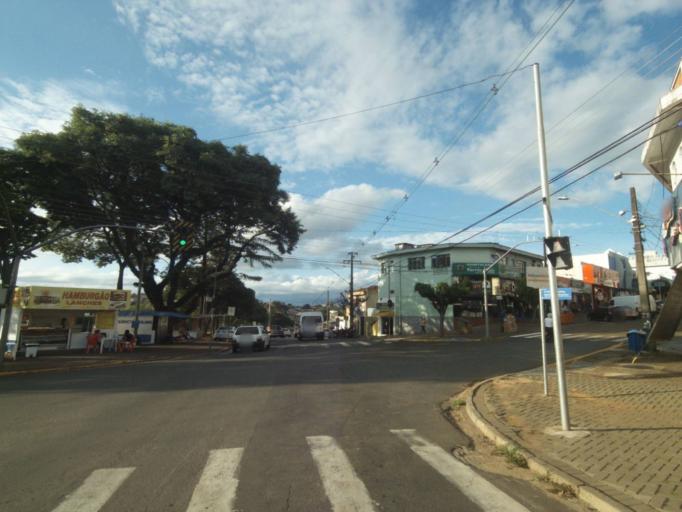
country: BR
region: Parana
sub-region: Telemaco Borba
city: Telemaco Borba
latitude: -24.3288
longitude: -50.6263
